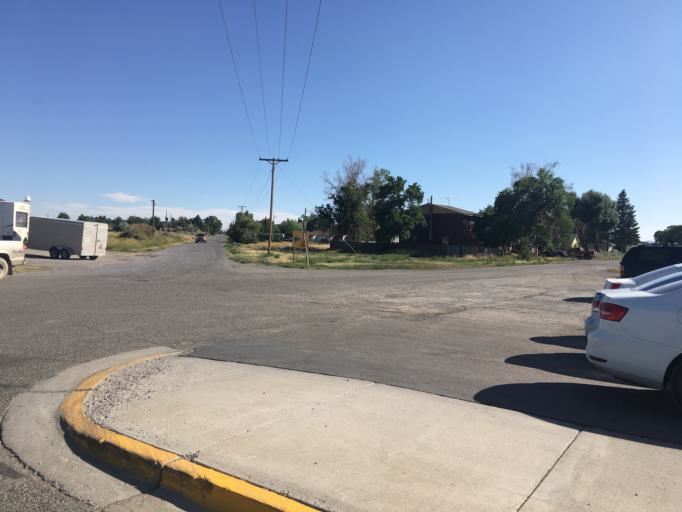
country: US
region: Idaho
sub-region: Butte County
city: Arco
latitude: 43.6334
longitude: -113.2962
